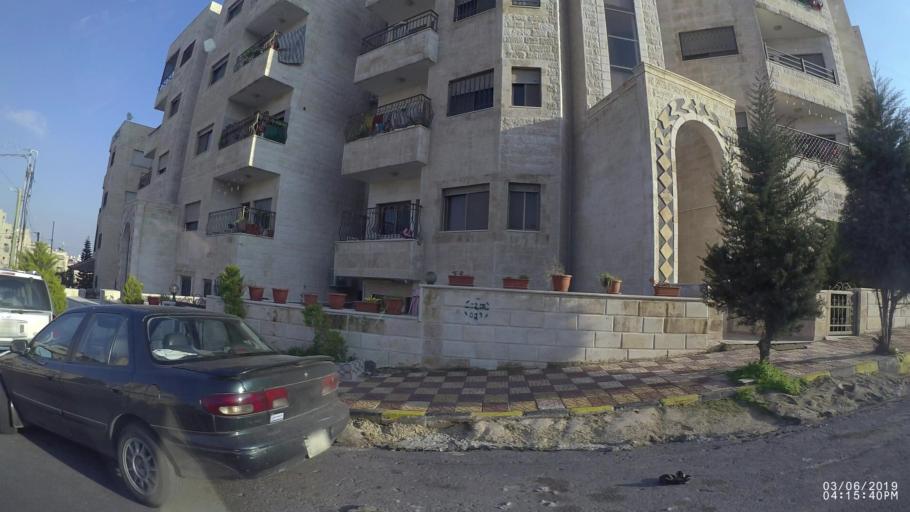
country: JO
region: Amman
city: Amman
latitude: 31.9860
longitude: 35.9430
